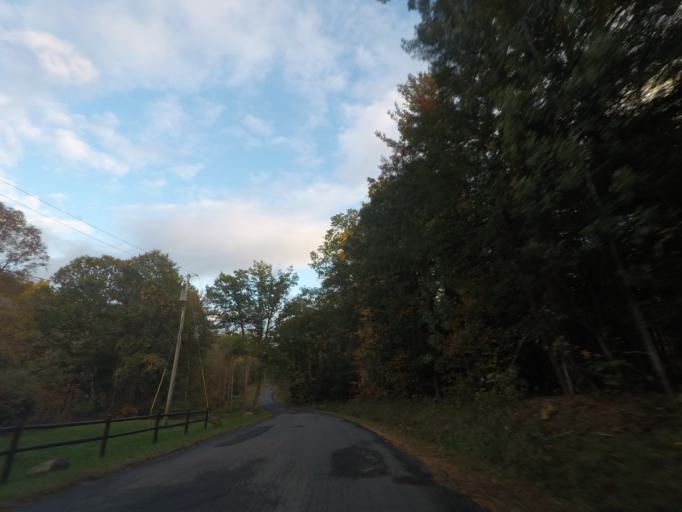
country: US
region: New York
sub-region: Rensselaer County
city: Nassau
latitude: 42.5405
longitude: -73.5792
